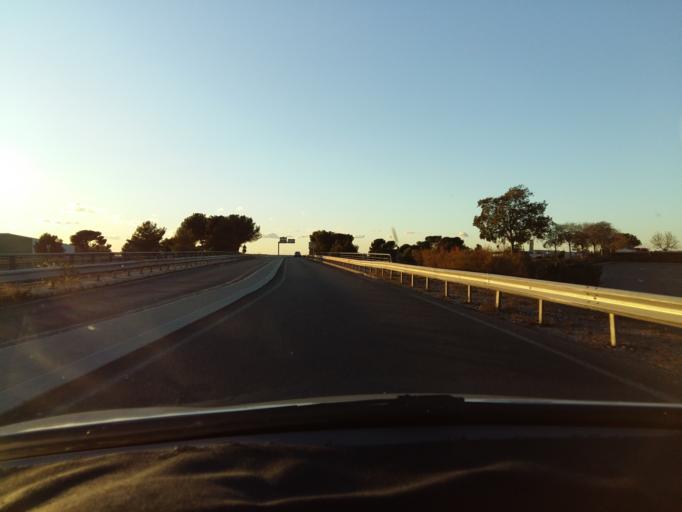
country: FR
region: Provence-Alpes-Cote d'Azur
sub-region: Departement des Bouches-du-Rhone
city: Vitrolles
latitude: 43.4404
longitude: 5.2497
